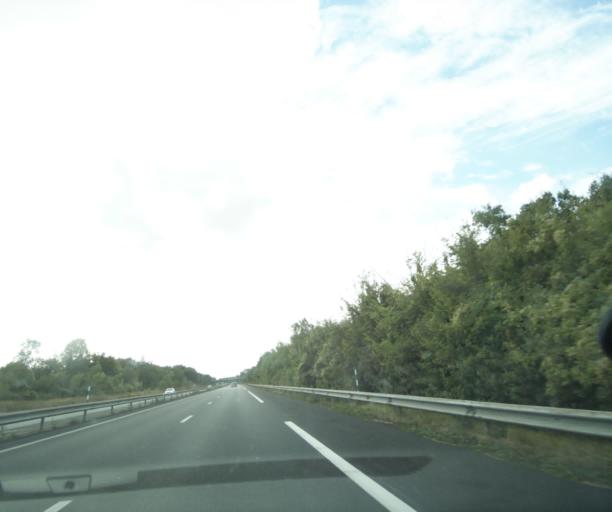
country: FR
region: Poitou-Charentes
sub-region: Departement de la Charente-Maritime
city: Thenac
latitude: 45.6604
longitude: -0.6358
